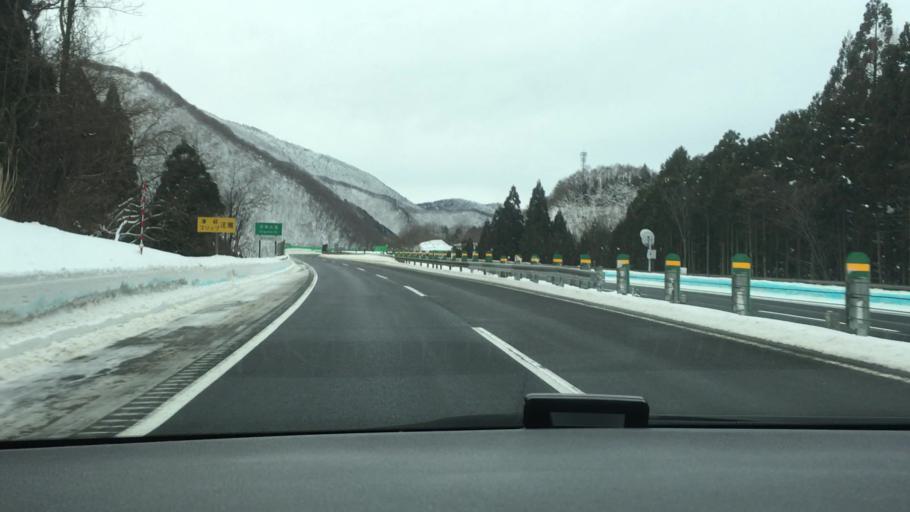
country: JP
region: Akita
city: Hanawa
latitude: 40.1204
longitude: 140.8501
